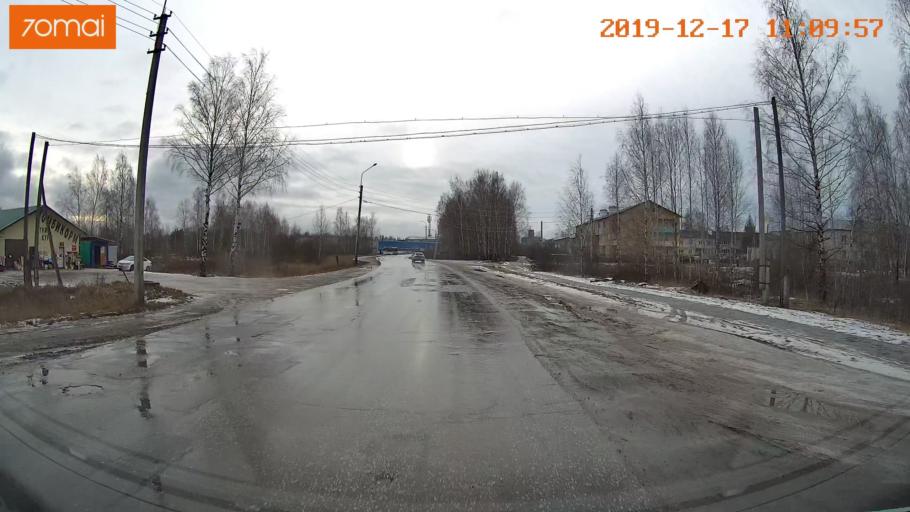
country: RU
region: Vladimir
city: Gus'-Khrustal'nyy
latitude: 55.5965
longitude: 40.6413
